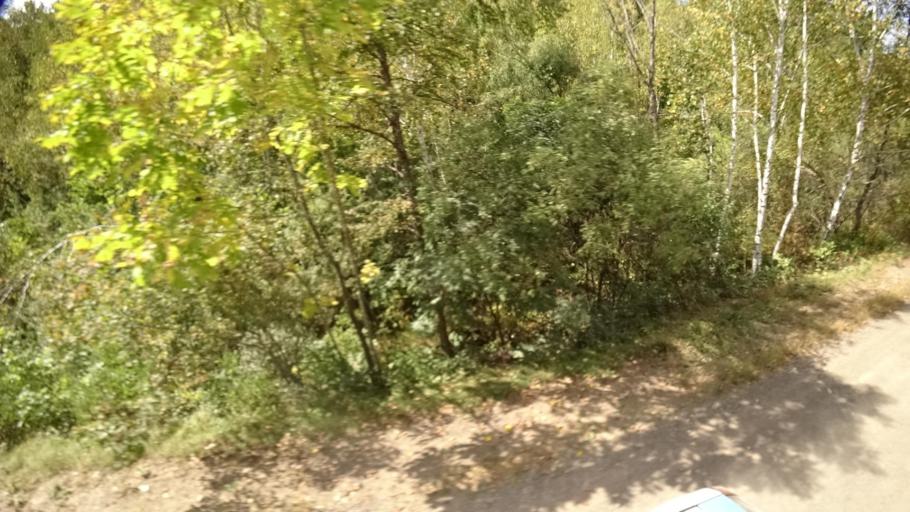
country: RU
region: Primorskiy
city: Yakovlevka
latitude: 44.7021
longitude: 133.6518
